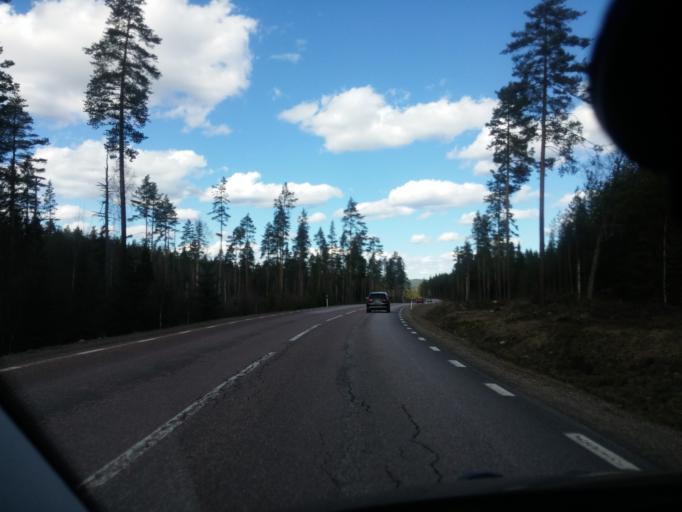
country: SE
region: Dalarna
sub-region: Faluns Kommun
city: Svardsjo
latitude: 60.7760
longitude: 15.7535
